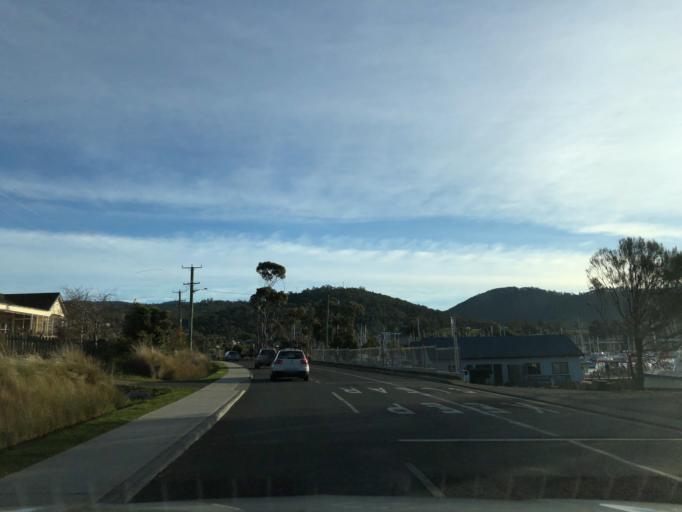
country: AU
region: Tasmania
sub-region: Kingborough
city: Kettering
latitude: -43.1275
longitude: 147.2547
